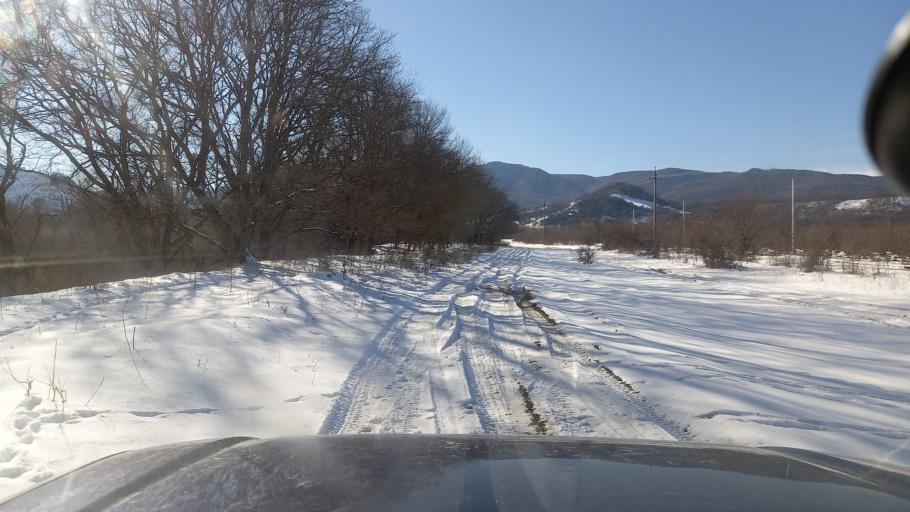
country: RU
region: Adygeya
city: Kamennomostskiy
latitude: 44.2171
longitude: 40.1767
